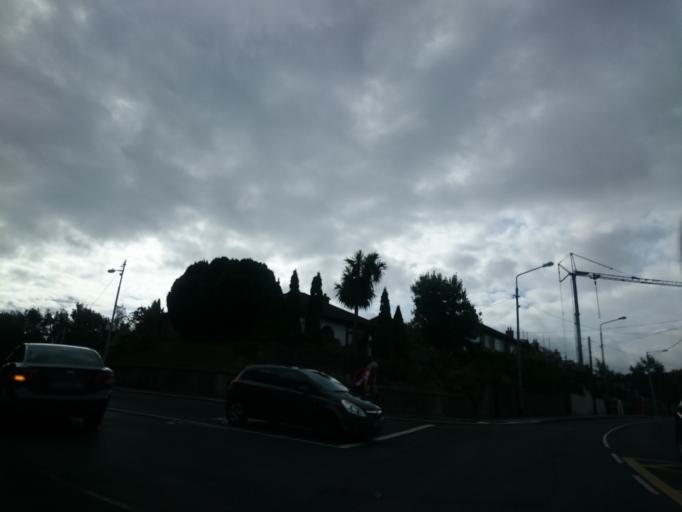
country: IE
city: Milltown
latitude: 53.3098
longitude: -6.2467
